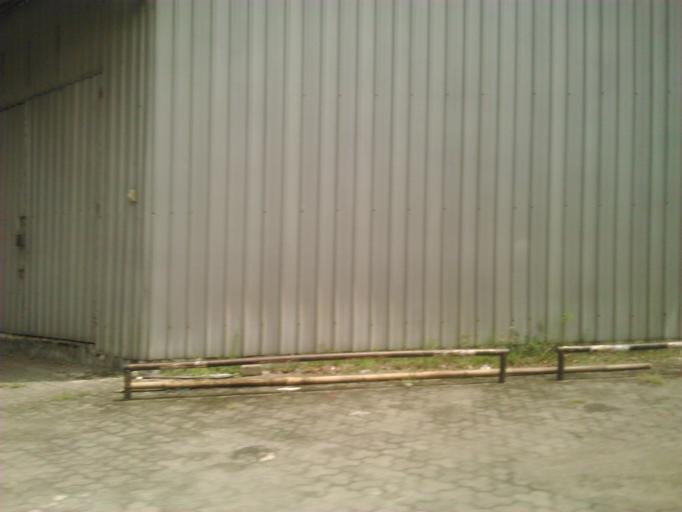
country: ID
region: East Java
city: Pacarkeling
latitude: -7.2637
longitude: 112.7496
